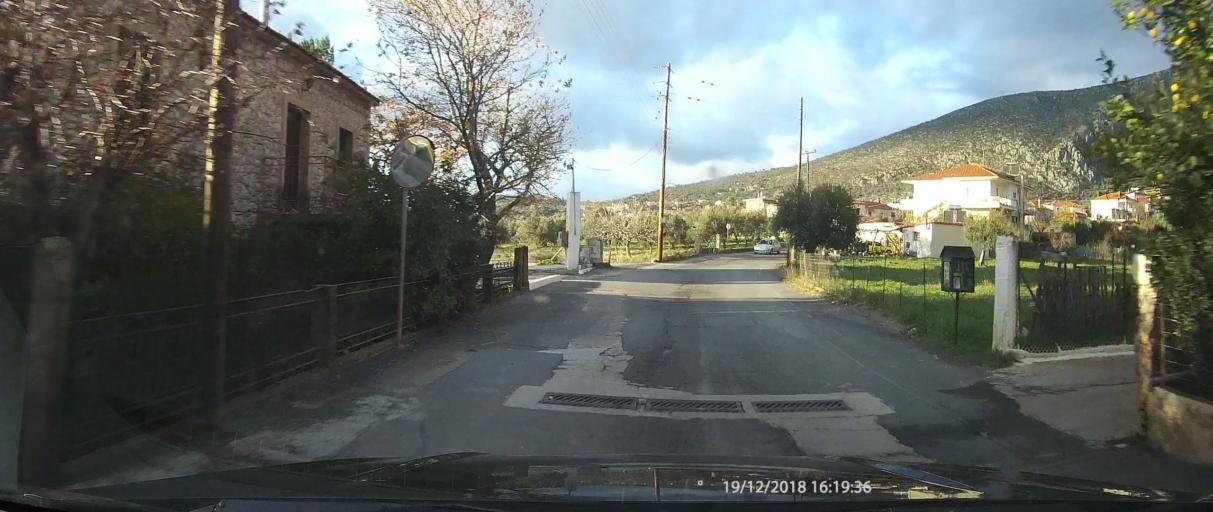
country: GR
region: Peloponnese
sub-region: Nomos Lakonias
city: Kato Glikovrisi
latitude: 36.9327
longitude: 22.8211
